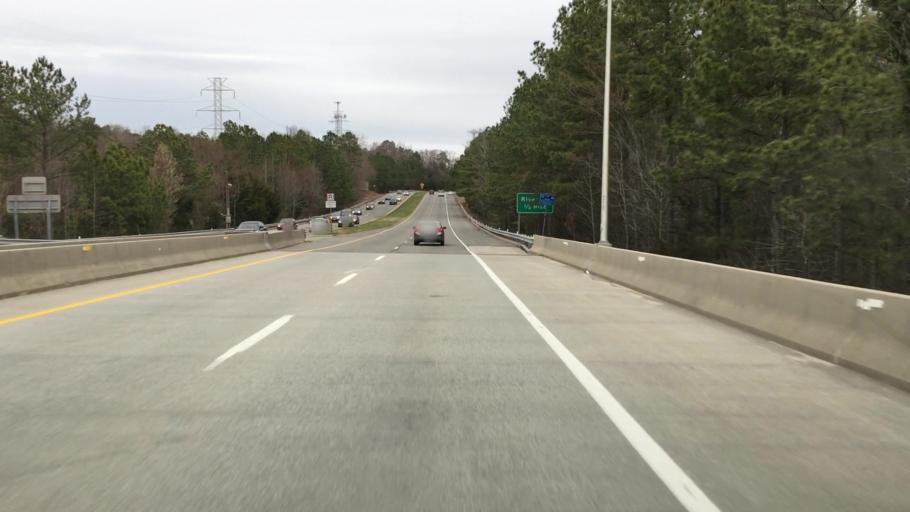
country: US
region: Virginia
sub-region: Henrico County
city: Tuckahoe
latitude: 37.5661
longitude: -77.5773
